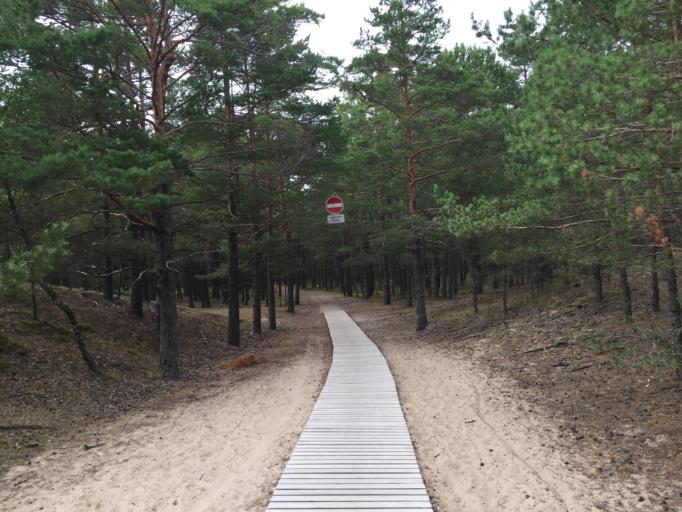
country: LV
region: Carnikava
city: Carnikava
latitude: 57.1365
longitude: 24.2466
